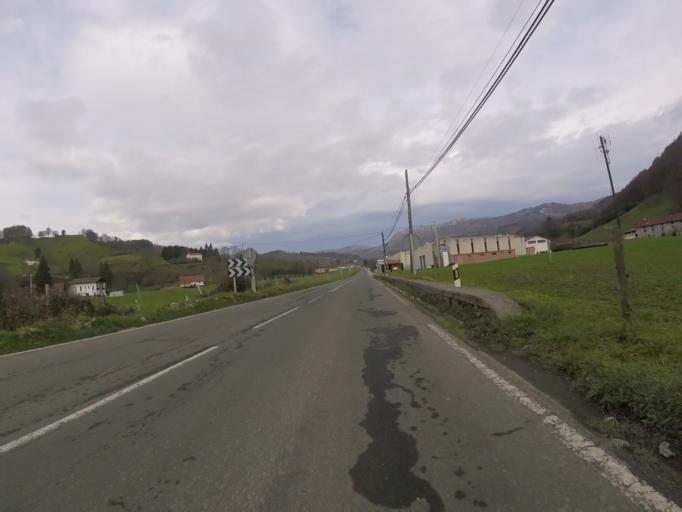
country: ES
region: Basque Country
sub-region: Provincia de Guipuzcoa
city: Albiztur
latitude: 43.1307
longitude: -2.1593
